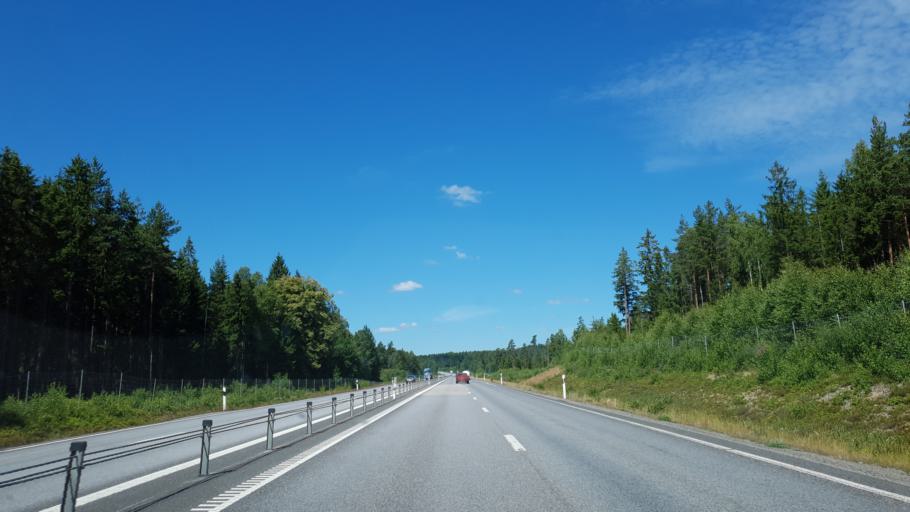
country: SE
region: Kronoberg
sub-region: Vaxjo Kommun
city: Gemla
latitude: 56.9141
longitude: 14.6274
